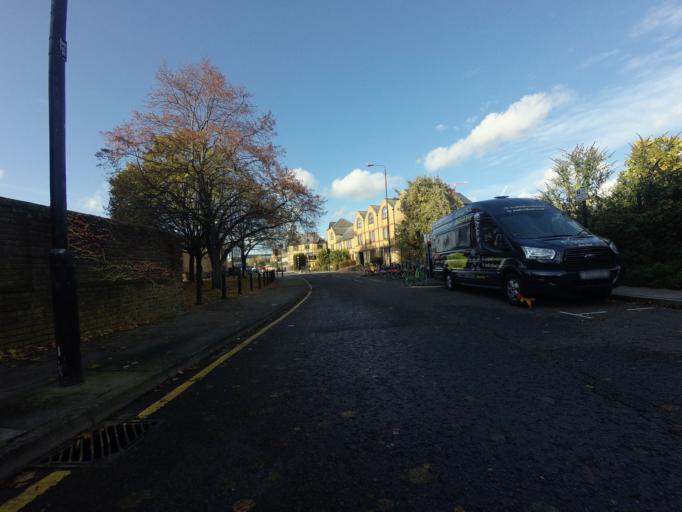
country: GB
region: England
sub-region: Greater London
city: Bethnal Green
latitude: 51.5046
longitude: -0.0634
